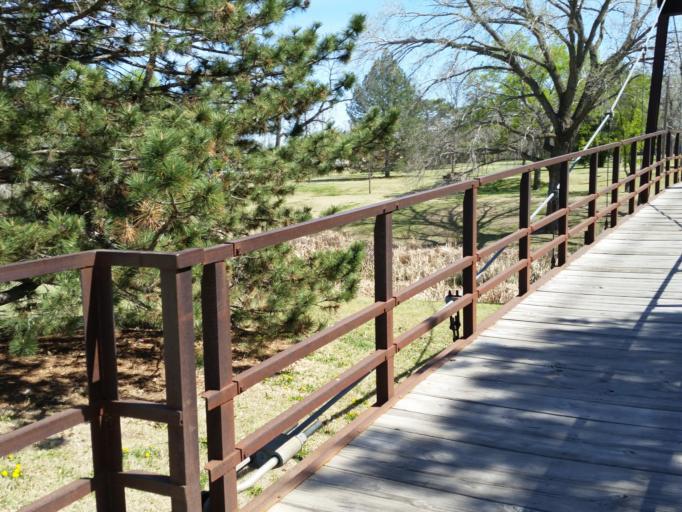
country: US
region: Kansas
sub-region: Saline County
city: Salina
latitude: 38.8331
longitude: -97.6042
